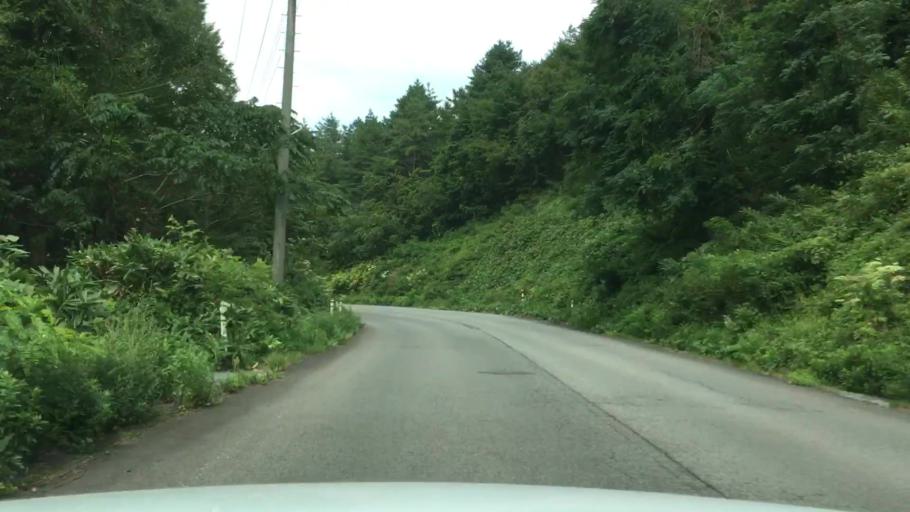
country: JP
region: Aomori
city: Shimokizukuri
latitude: 40.7243
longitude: 140.2565
